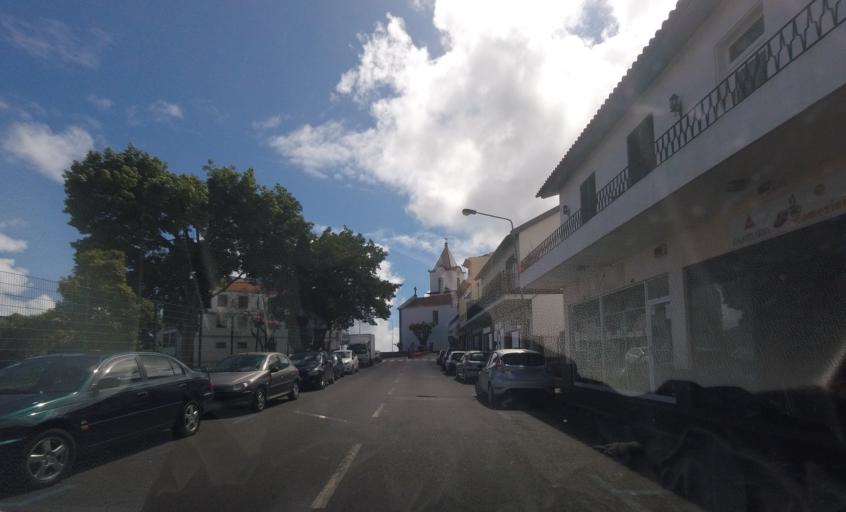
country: PT
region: Madeira
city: Camara de Lobos
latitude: 32.6718
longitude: -16.9792
